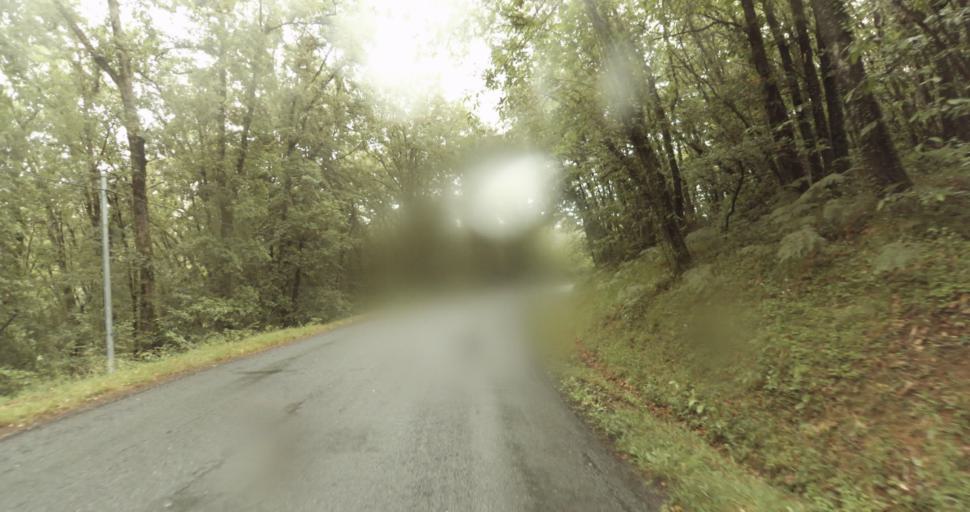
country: FR
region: Aquitaine
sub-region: Departement de la Dordogne
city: Le Bugue
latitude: 44.8134
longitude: 0.8813
